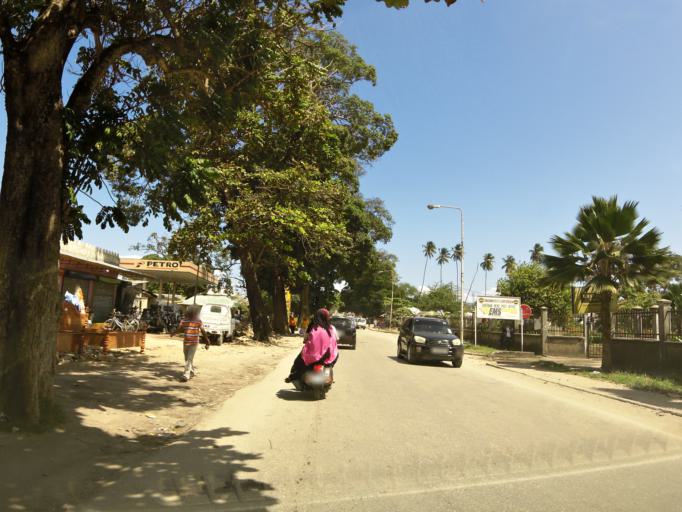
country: TZ
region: Zanzibar Urban/West
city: Zanzibar
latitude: -6.1651
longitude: 39.2056
